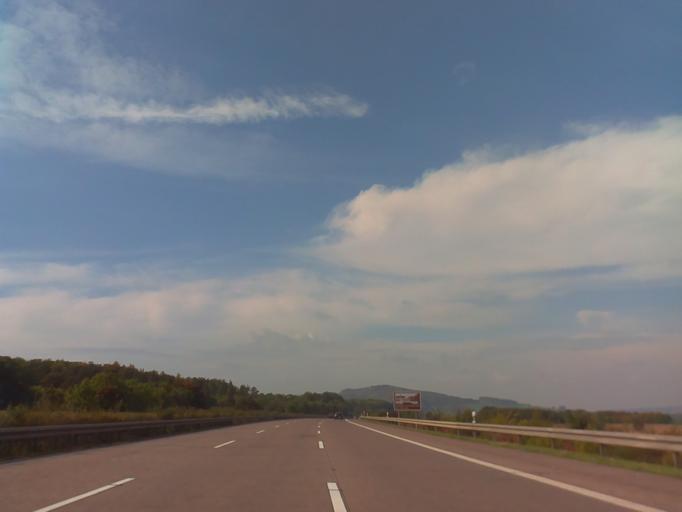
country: DE
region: Thuringia
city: Mechterstadt
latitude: 50.9257
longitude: 10.5155
